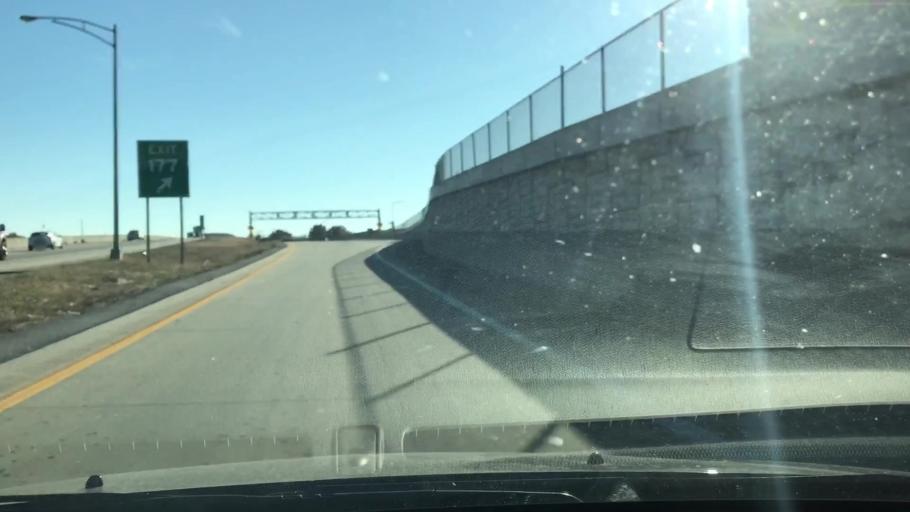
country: US
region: Missouri
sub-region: Jackson County
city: Grandview
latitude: 38.8608
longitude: -94.5277
